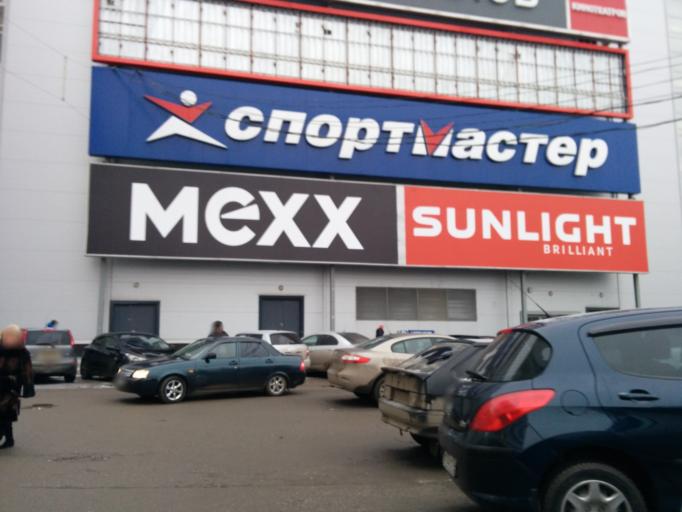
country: RU
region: Perm
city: Perm
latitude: 58.0094
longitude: 56.2360
